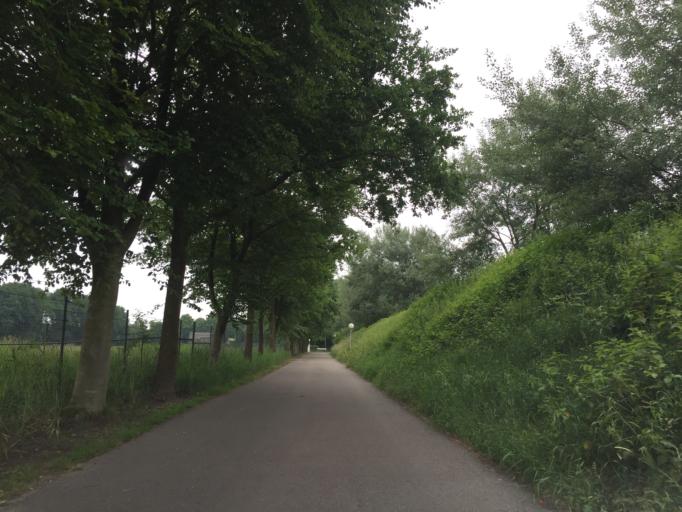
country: NL
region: North Brabant
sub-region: Gemeente Maasdonk
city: Geffen
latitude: 51.7136
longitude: 5.4197
